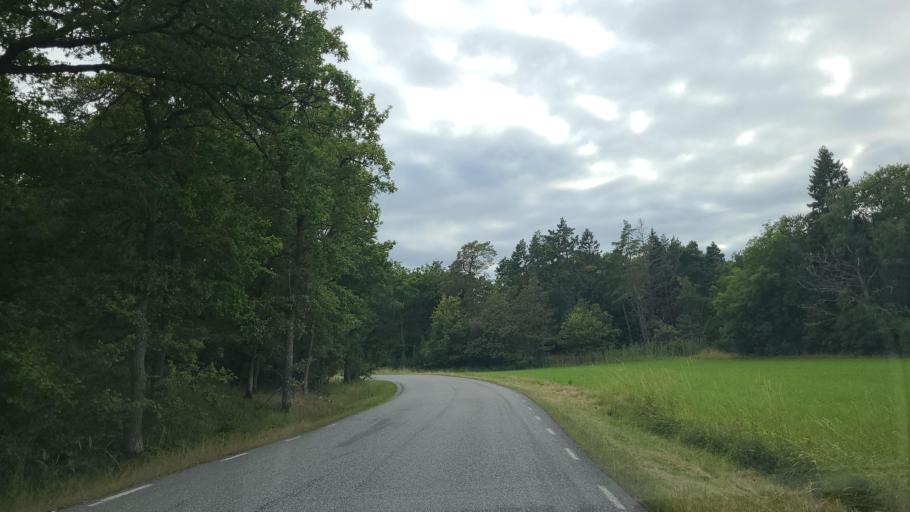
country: SE
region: Stockholm
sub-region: Upplands-Bro Kommun
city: Bro
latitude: 59.4718
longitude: 17.5938
